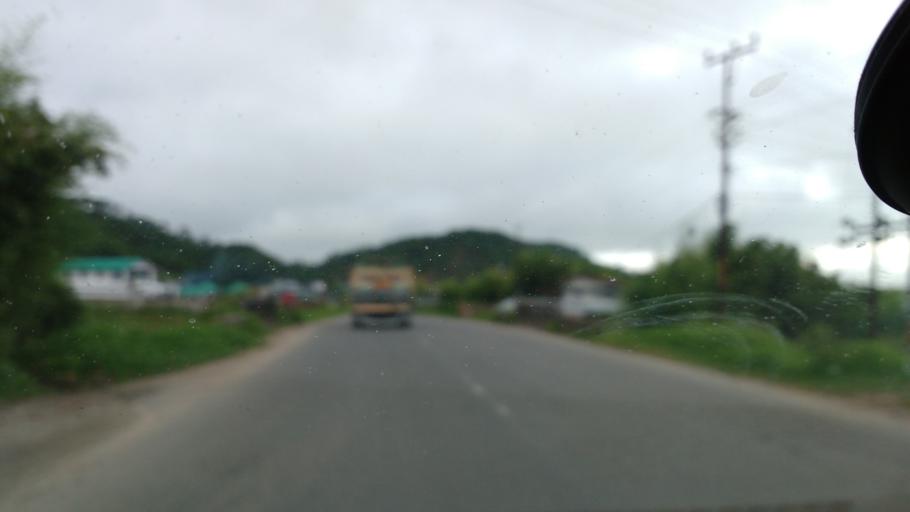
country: IN
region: Meghalaya
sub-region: East Khasi Hills
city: Shillong
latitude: 25.5232
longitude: 91.8172
